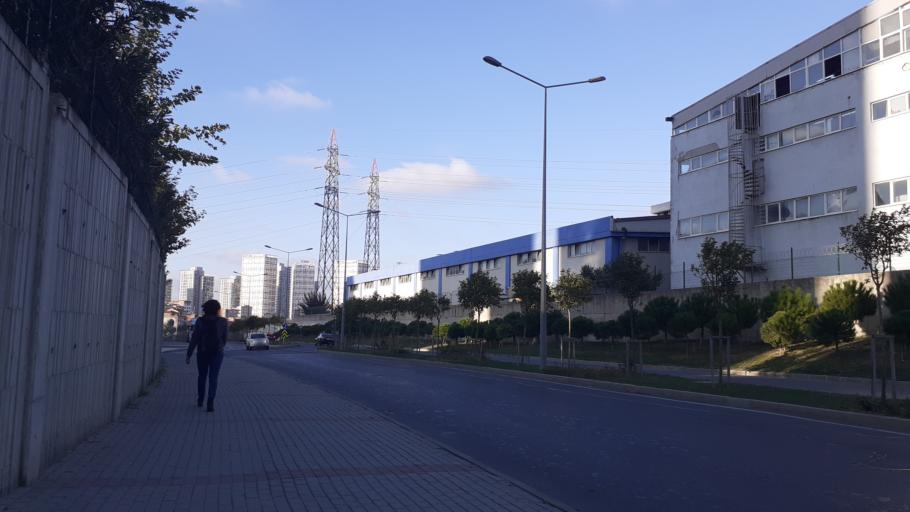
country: TR
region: Istanbul
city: Basaksehir
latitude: 41.0661
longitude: 28.7808
